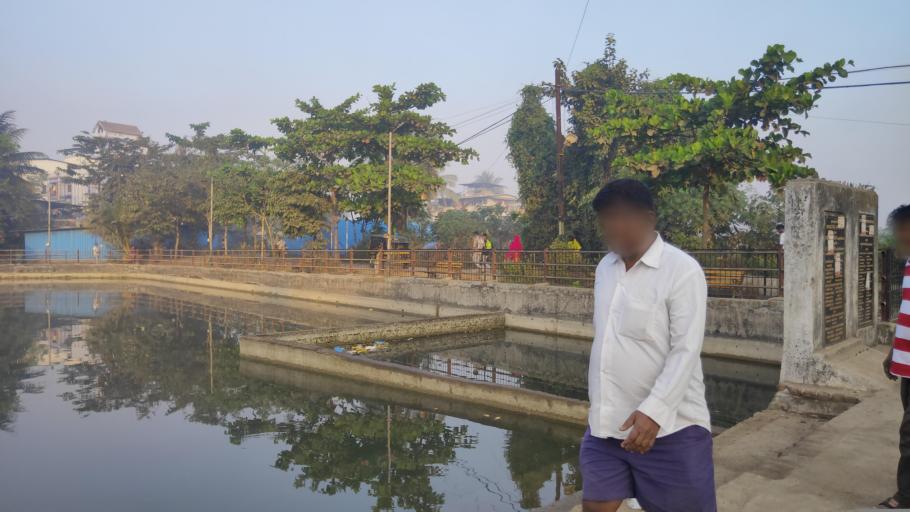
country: IN
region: Maharashtra
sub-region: Thane
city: Bhiwandi
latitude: 19.2556
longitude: 73.0201
